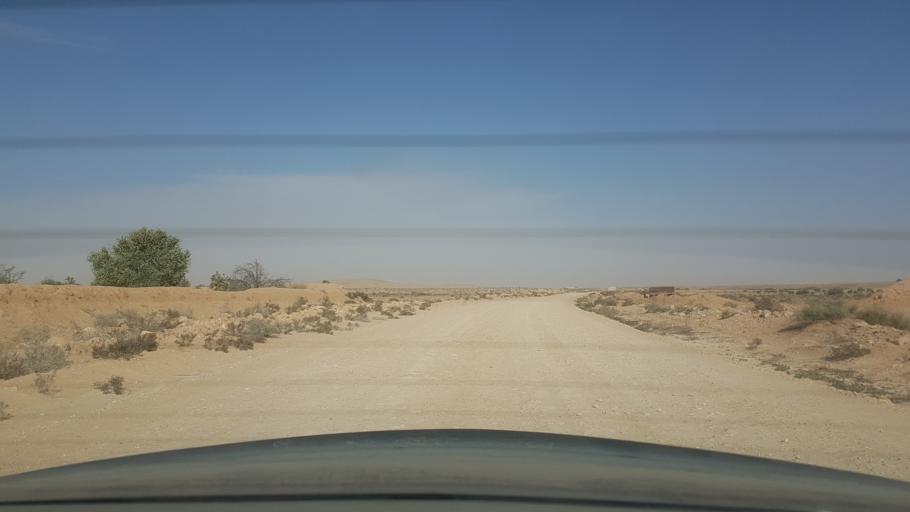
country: TN
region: Qabis
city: El Hamma
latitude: 33.6637
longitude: 9.7352
